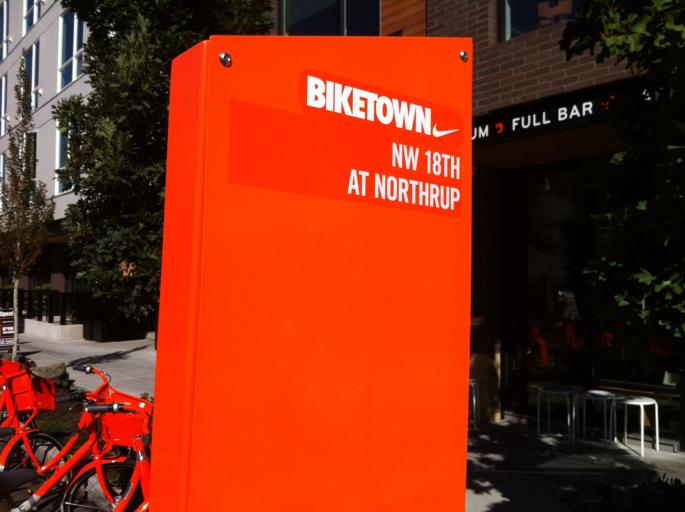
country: US
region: Oregon
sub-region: Multnomah County
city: Portland
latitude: 45.5315
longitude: -122.6895
